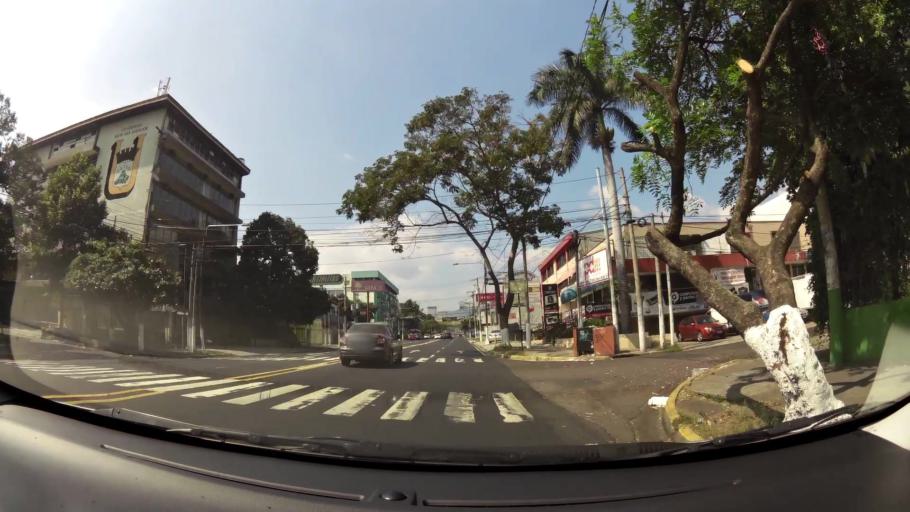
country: SV
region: San Salvador
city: San Salvador
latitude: 13.7003
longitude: -89.2123
